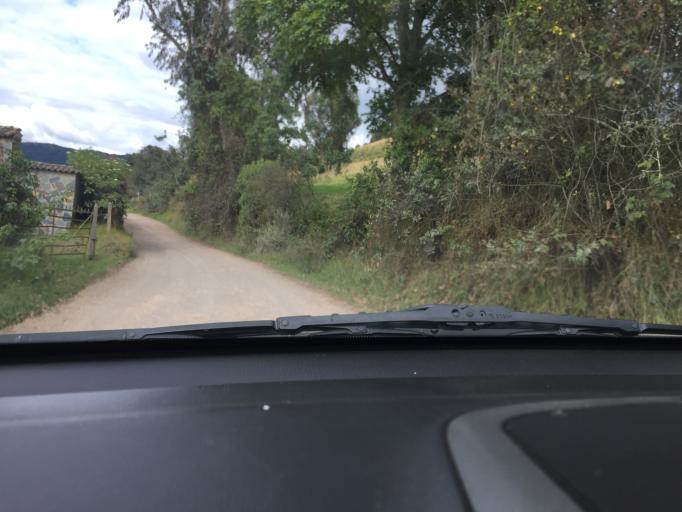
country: CO
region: Cundinamarca
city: Subachoque
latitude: 4.9332
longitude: -74.1541
